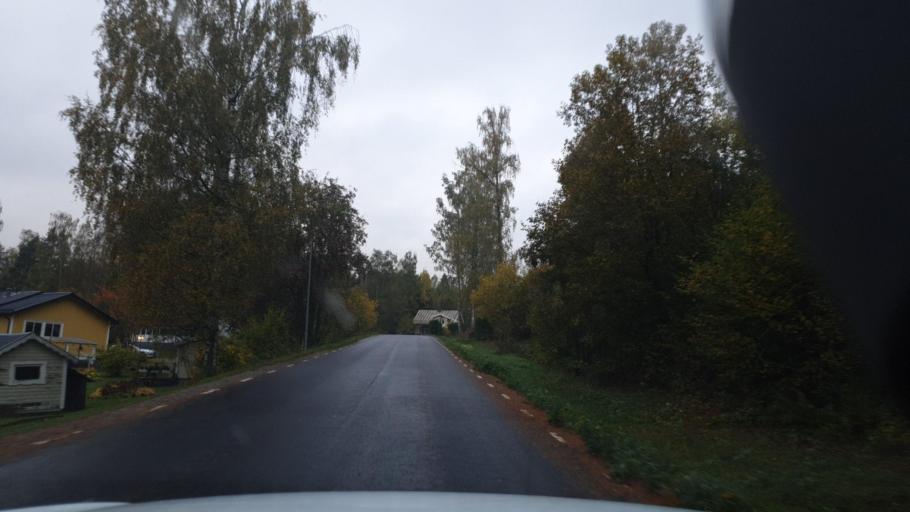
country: SE
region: Vaermland
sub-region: Arvika Kommun
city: Arvika
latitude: 59.6484
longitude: 12.7463
